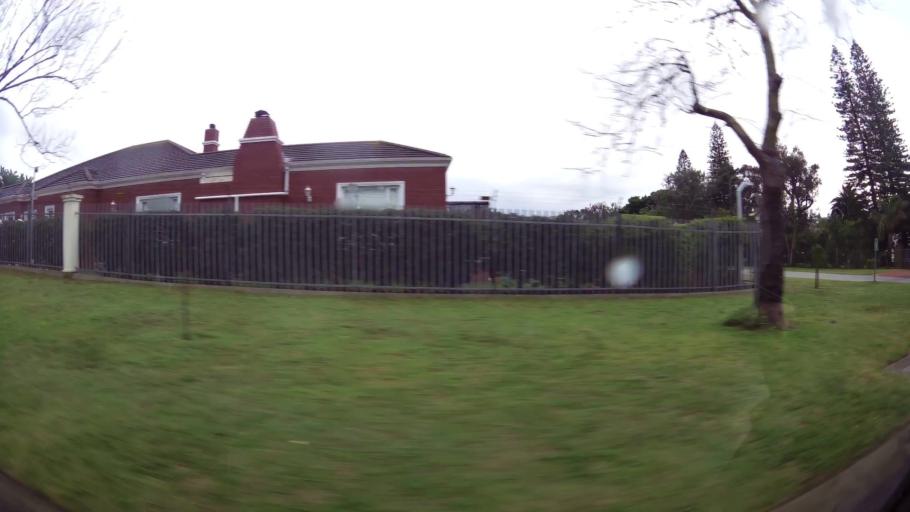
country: ZA
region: Eastern Cape
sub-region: Nelson Mandela Bay Metropolitan Municipality
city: Port Elizabeth
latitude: -33.9739
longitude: 25.5797
